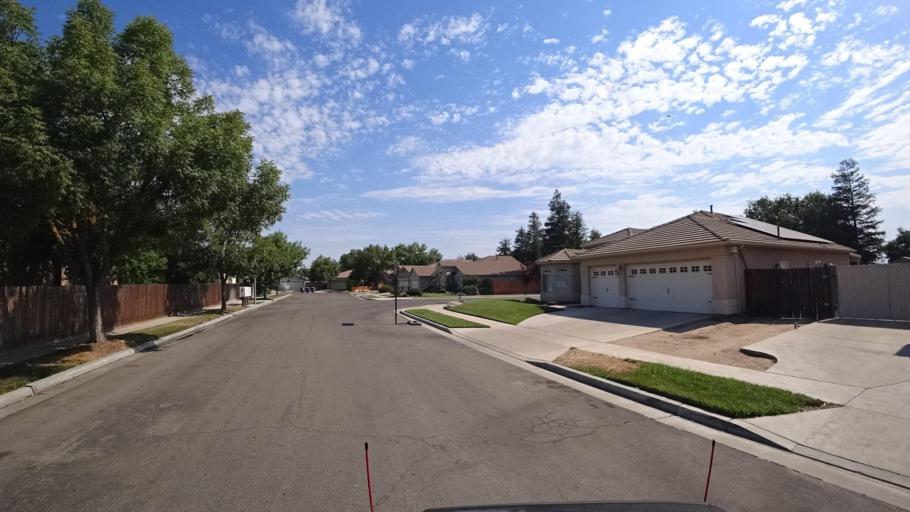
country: US
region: California
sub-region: Fresno County
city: Sunnyside
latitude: 36.7156
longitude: -119.6916
